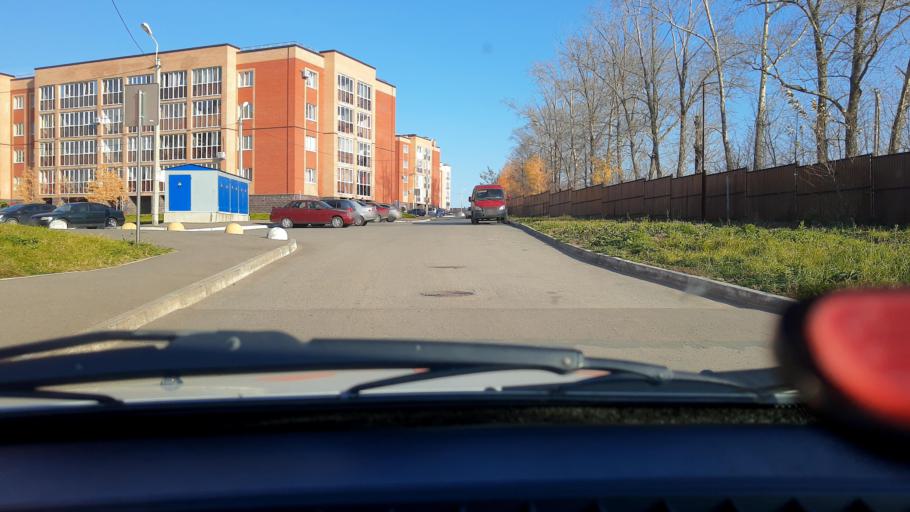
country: RU
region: Bashkortostan
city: Mikhaylovka
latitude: 54.8278
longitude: 55.8611
